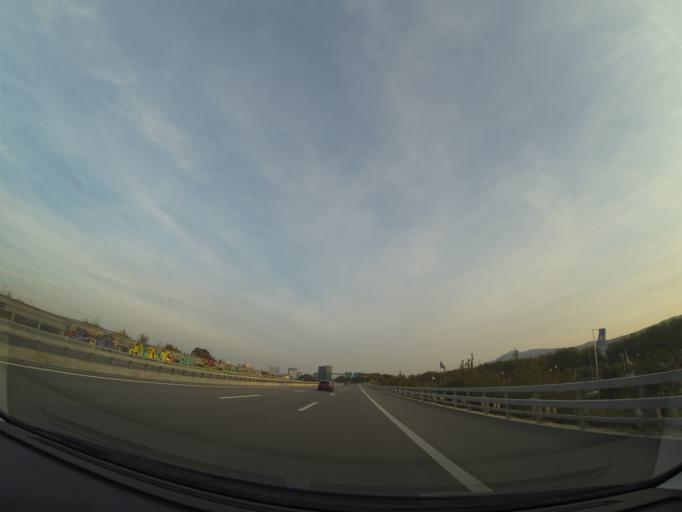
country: CH
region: Zurich
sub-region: Bezirk Dietikon
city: Oberengstringen
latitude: 47.4016
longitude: 8.4710
